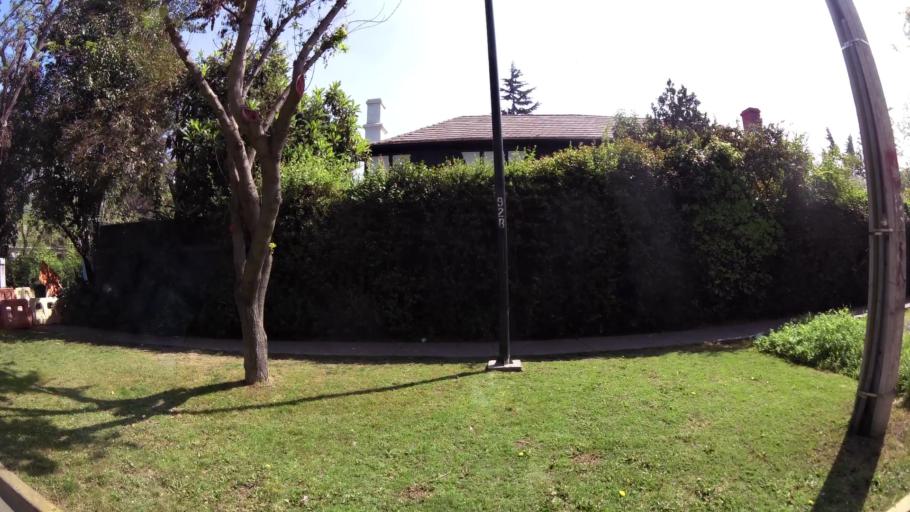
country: CL
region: Santiago Metropolitan
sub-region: Provincia de Santiago
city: Villa Presidente Frei, Nunoa, Santiago, Chile
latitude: -33.3994
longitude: -70.5957
